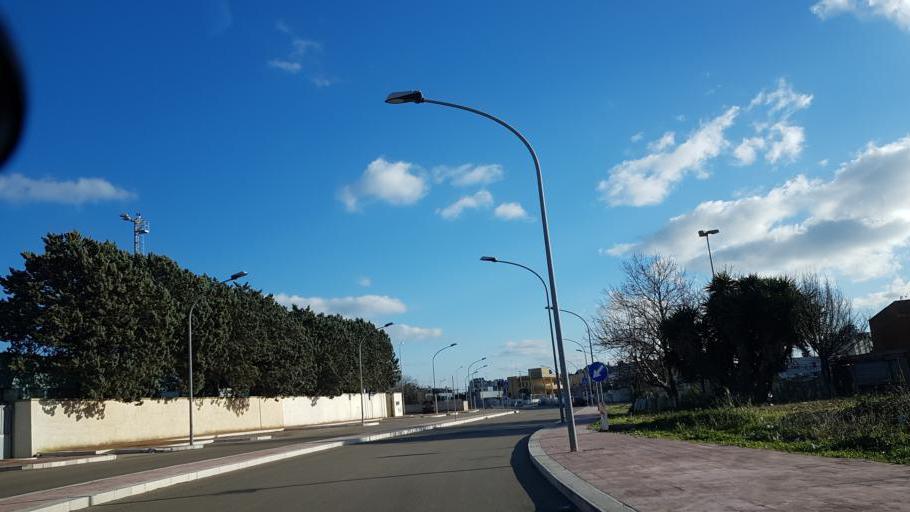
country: IT
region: Apulia
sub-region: Provincia di Brindisi
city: Brindisi
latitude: 40.6471
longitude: 17.9215
